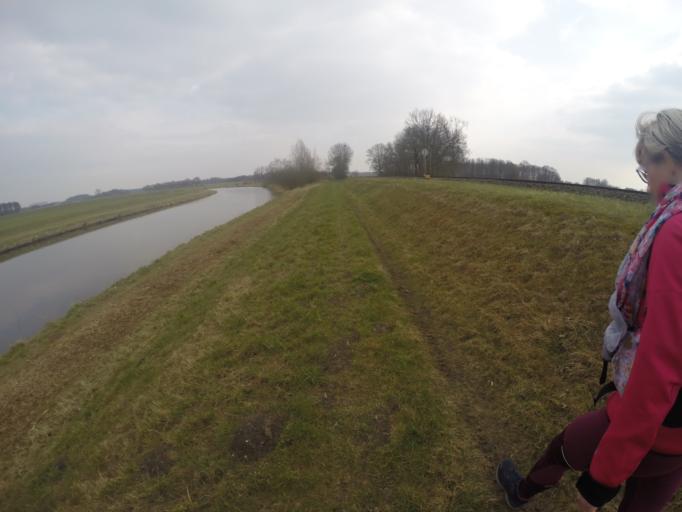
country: NL
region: Gelderland
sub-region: Gemeente Zutphen
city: Warnsveld
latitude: 52.1491
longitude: 6.2639
